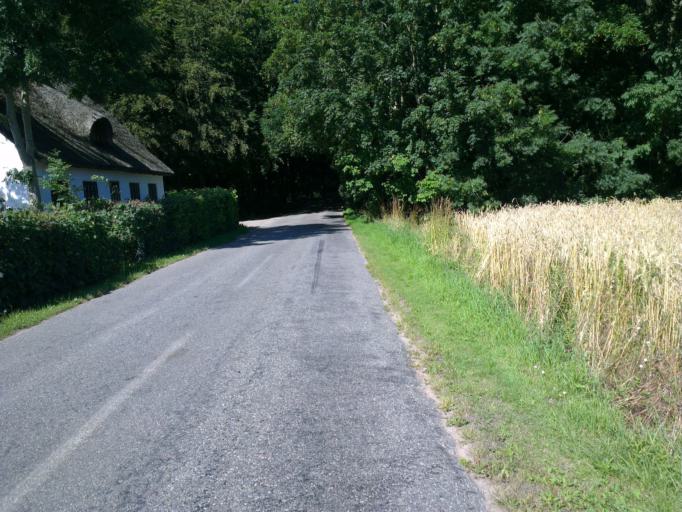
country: DK
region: Capital Region
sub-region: Frederikssund Kommune
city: Skibby
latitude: 55.7169
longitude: 11.9505
